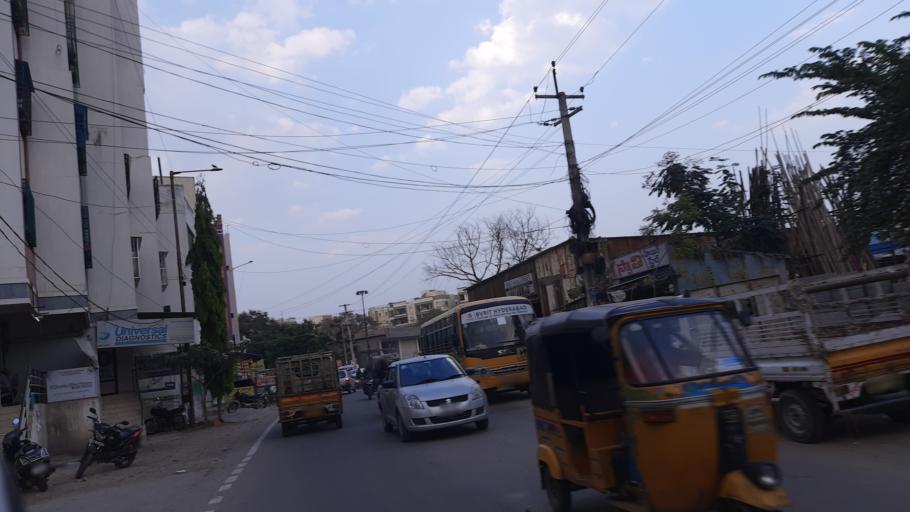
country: IN
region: Telangana
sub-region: Rangareddi
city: Kukatpalli
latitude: 17.4960
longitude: 78.4168
